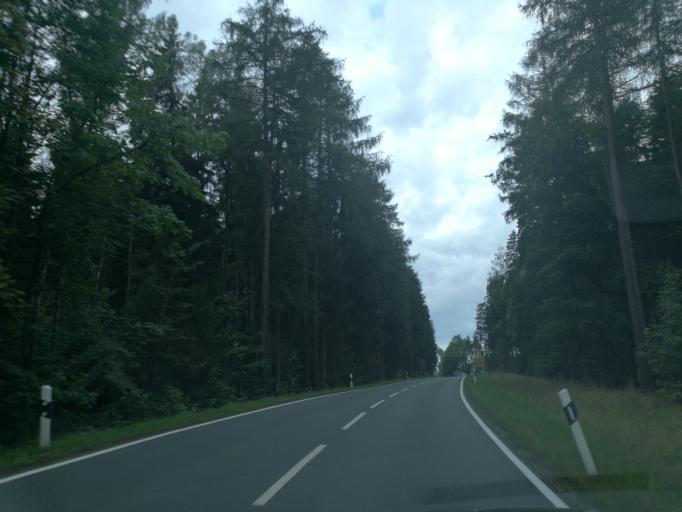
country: DE
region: Saxony
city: Eichigt
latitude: 50.3347
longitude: 12.1623
